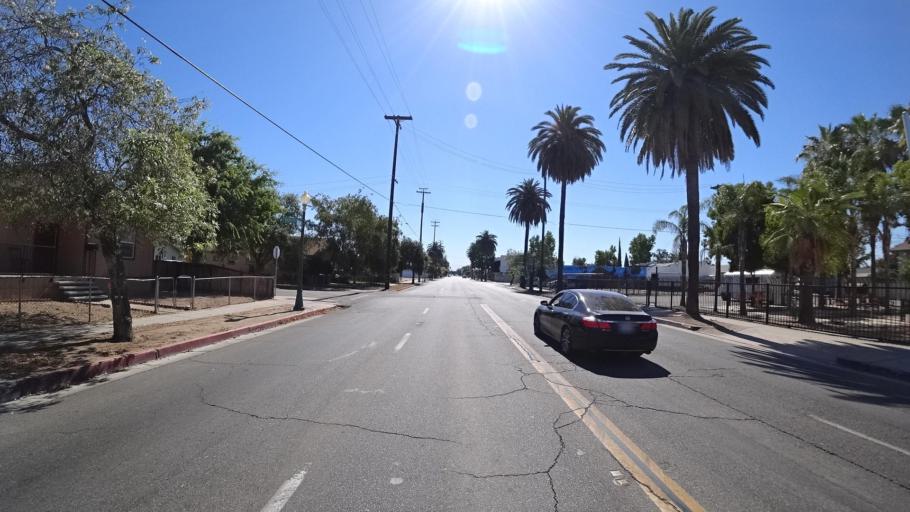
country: US
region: California
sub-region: Fresno County
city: Fresno
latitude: 36.7504
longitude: -119.8055
